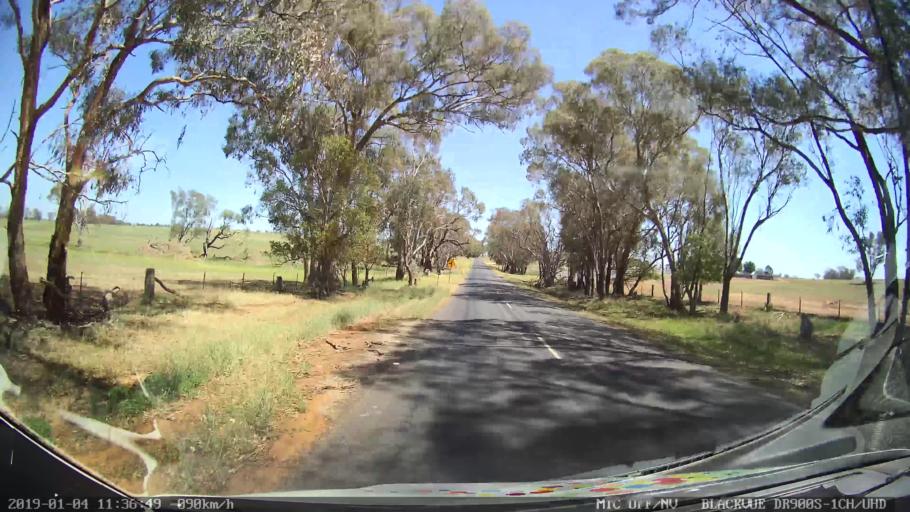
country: AU
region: New South Wales
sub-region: Cabonne
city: Molong
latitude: -33.0396
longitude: 148.8123
